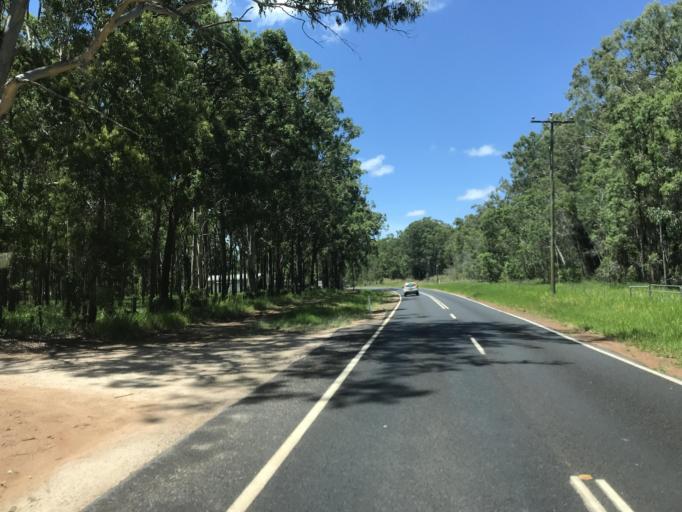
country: AU
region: Queensland
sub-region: Tablelands
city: Atherton
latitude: -17.4276
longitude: 145.3986
